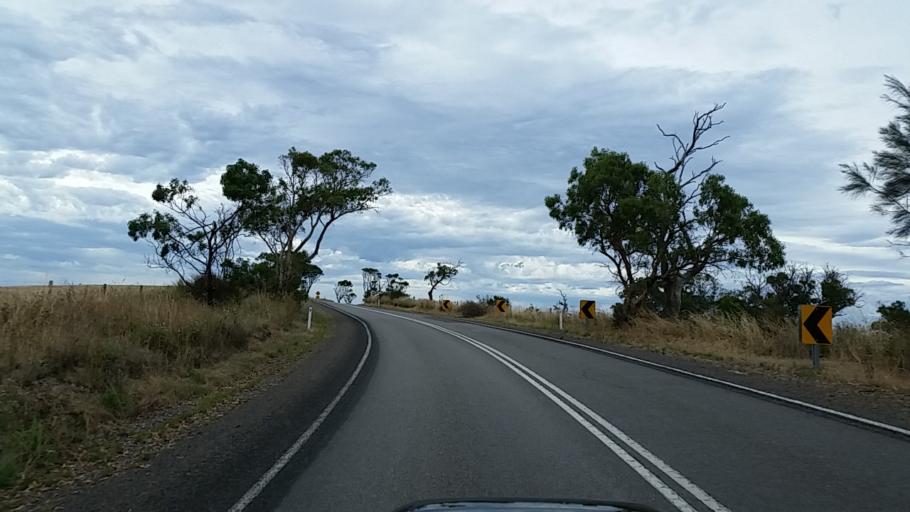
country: AU
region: South Australia
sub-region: Onkaparinga
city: Aldinga
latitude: -35.3759
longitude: 138.4556
